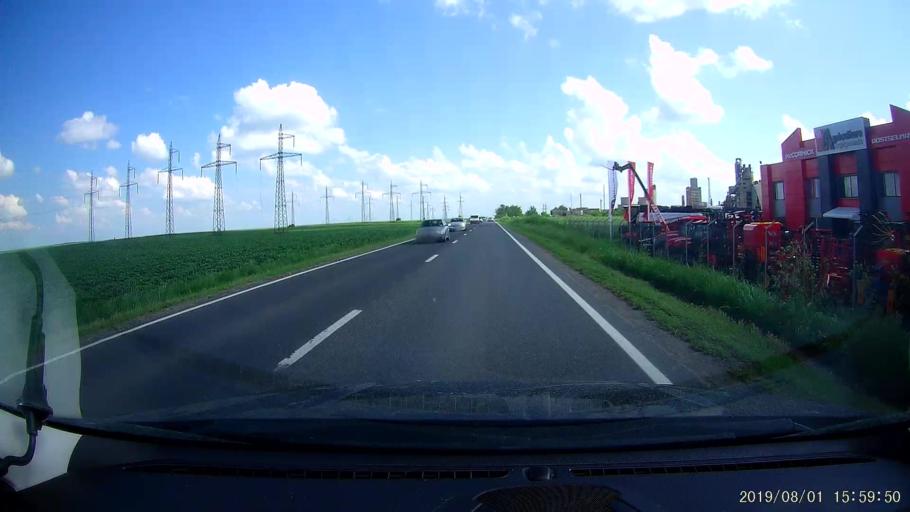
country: RO
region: Ialomita
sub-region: Comuna Slobozia
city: Slobozia
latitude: 44.5401
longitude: 27.3863
